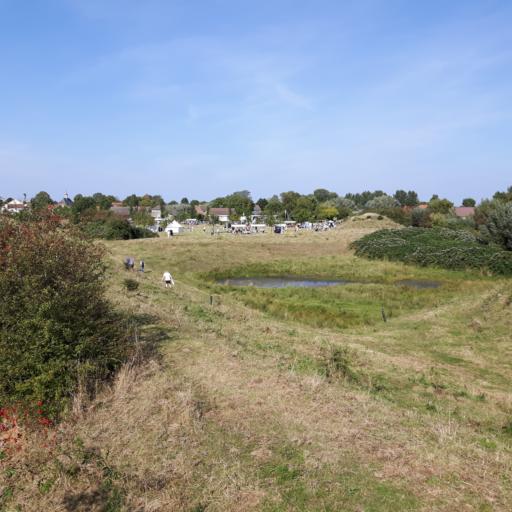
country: NL
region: Zeeland
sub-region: Gemeente Sluis
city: Sluis
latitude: 51.3427
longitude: 3.3865
